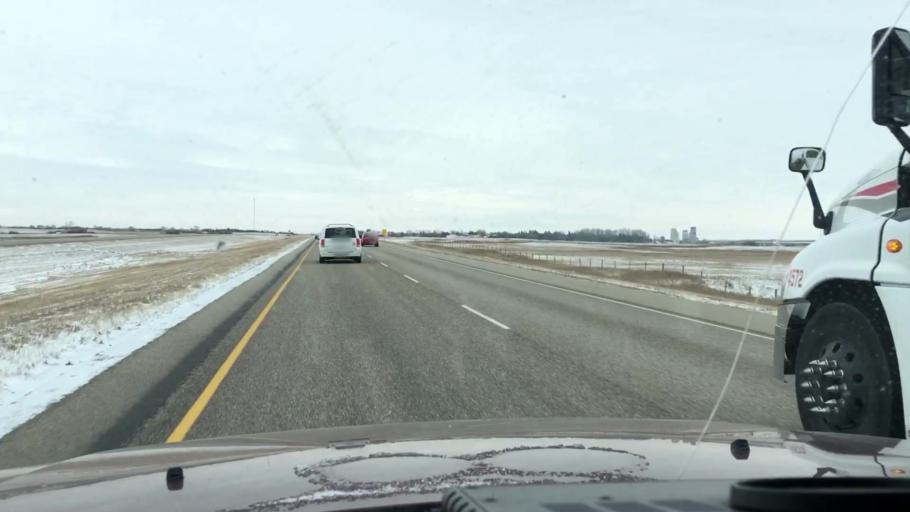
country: CA
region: Saskatchewan
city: Saskatoon
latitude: 51.5174
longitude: -106.2887
